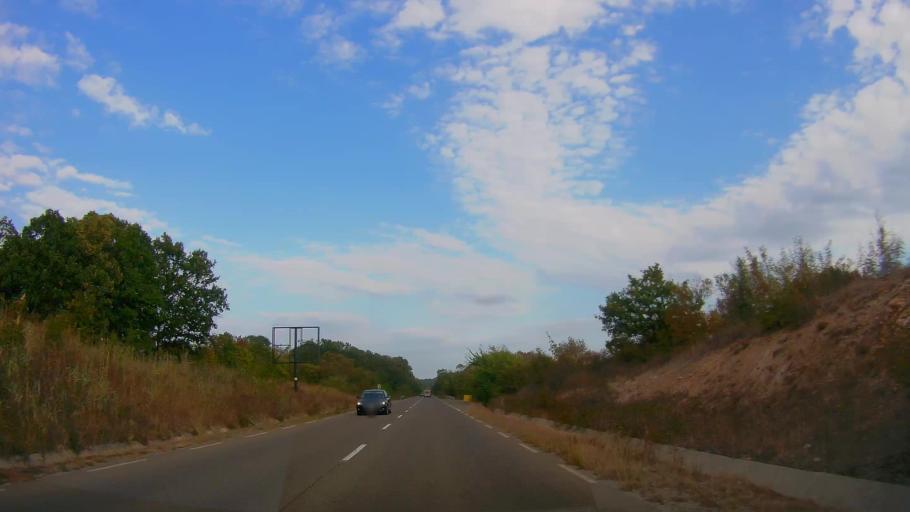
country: BG
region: Burgas
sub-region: Obshtina Sozopol
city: Sozopol
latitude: 42.3504
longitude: 27.7110
